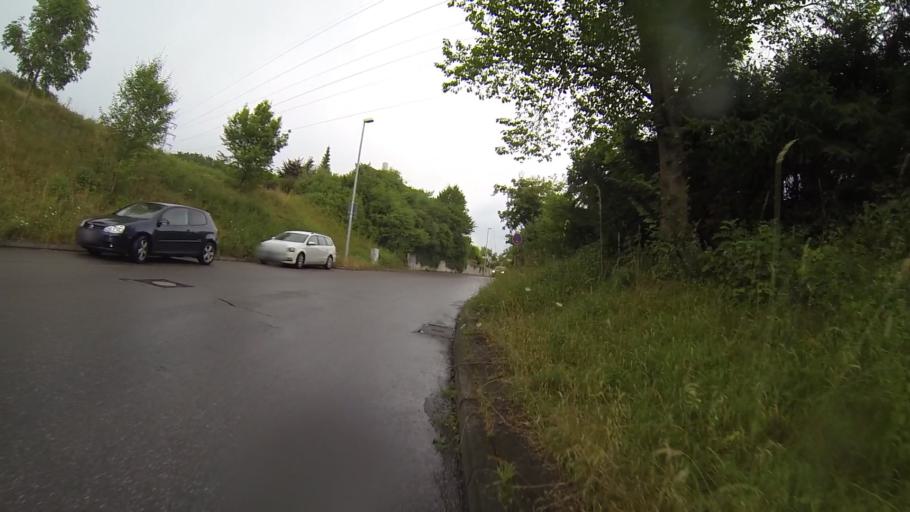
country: DE
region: Baden-Wuerttemberg
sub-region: Regierungsbezirk Stuttgart
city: Heidenheim an der Brenz
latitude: 48.6789
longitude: 10.1749
